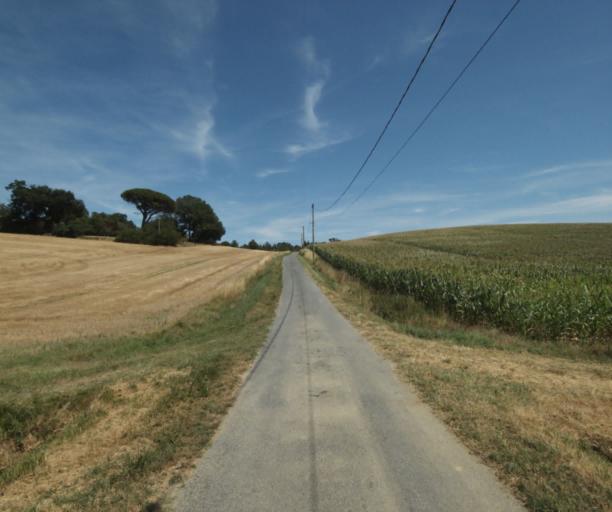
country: FR
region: Midi-Pyrenees
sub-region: Departement du Tarn
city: Puylaurens
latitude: 43.5366
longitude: 1.9957
